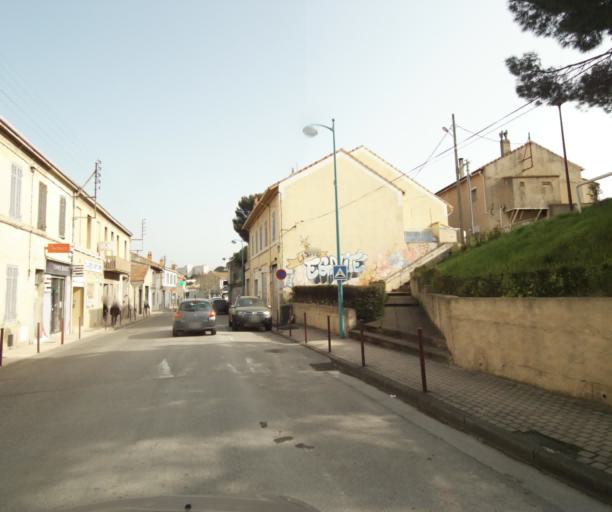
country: FR
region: Provence-Alpes-Cote d'Azur
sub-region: Departement des Bouches-du-Rhone
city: Marseille 15
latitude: 43.3801
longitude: 5.3495
